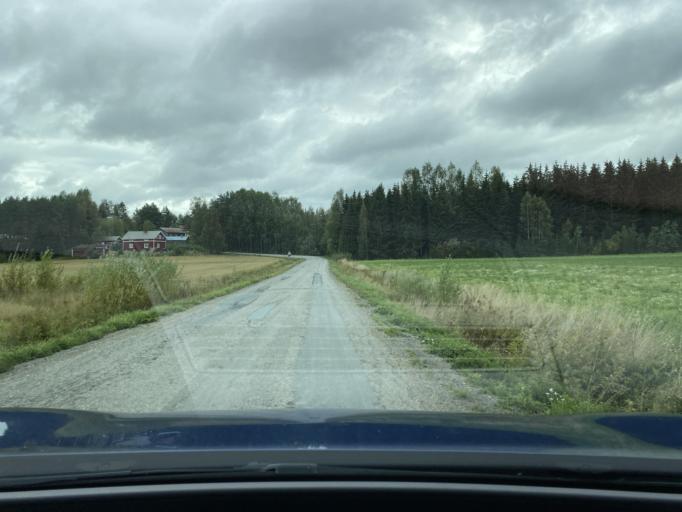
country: FI
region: Pirkanmaa
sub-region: Lounais-Pirkanmaa
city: Punkalaidun
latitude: 61.1702
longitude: 23.1790
